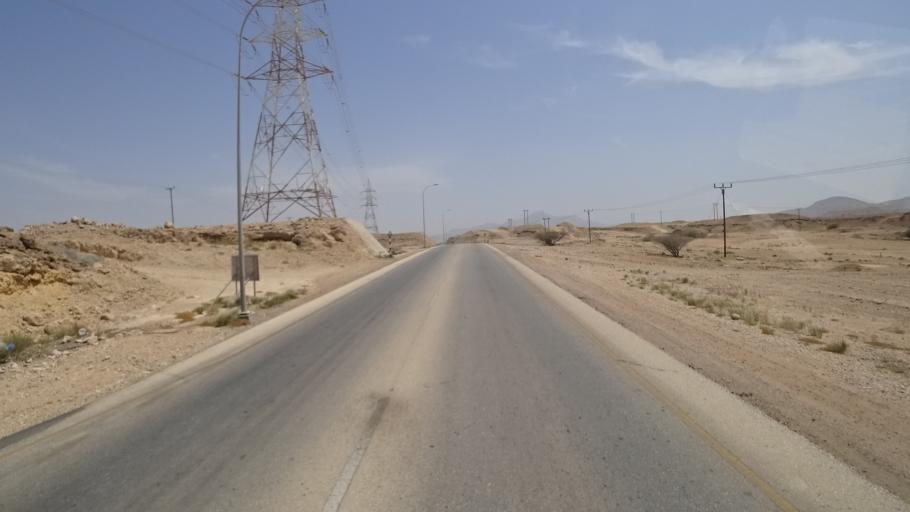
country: OM
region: Ash Sharqiyah
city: Sur
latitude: 22.5896
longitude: 59.4551
